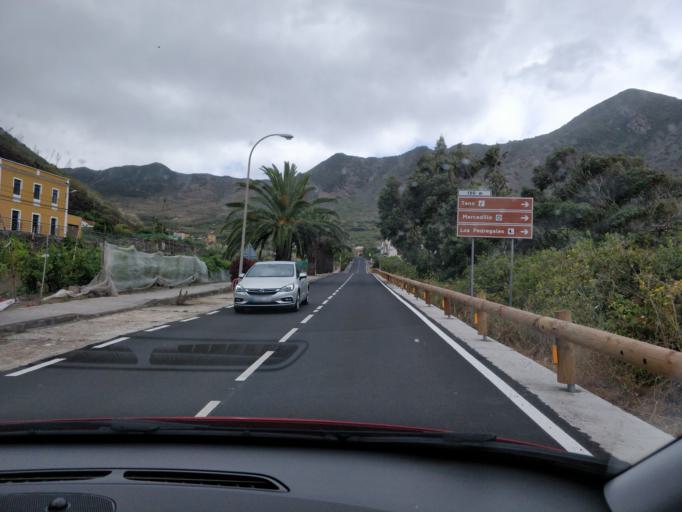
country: ES
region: Canary Islands
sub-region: Provincia de Santa Cruz de Tenerife
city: Tanque
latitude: 28.3418
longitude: -16.8496
